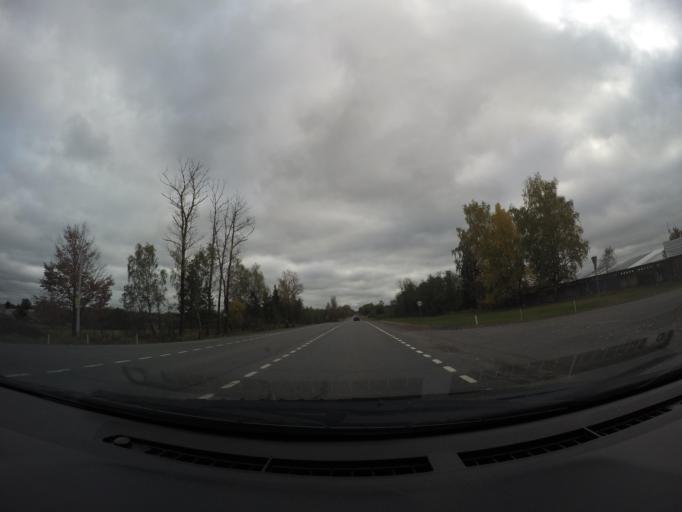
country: RU
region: Moskovskaya
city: Dorokhovo
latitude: 55.5952
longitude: 36.3627
